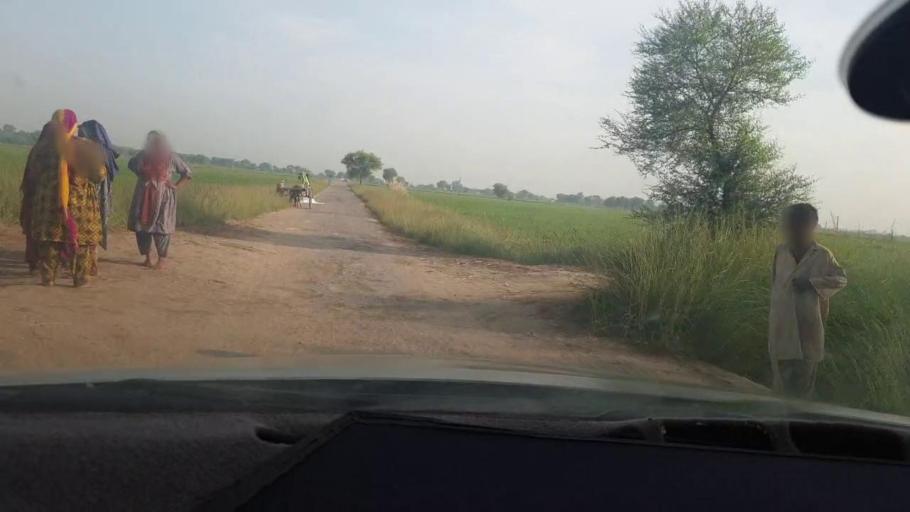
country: PK
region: Sindh
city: Jacobabad
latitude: 28.3028
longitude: 68.4149
